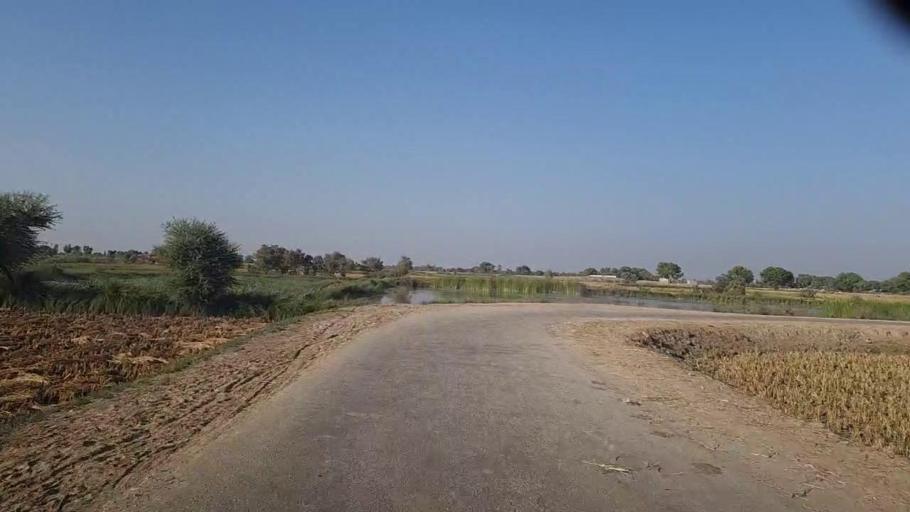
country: PK
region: Sindh
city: Tangwani
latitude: 28.2965
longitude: 68.9505
